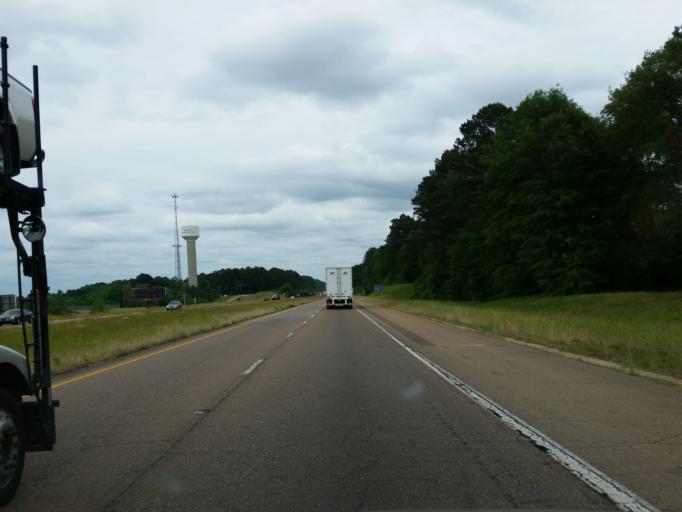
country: US
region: Mississippi
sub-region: Lauderdale County
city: Marion
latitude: 32.3847
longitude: -88.6285
